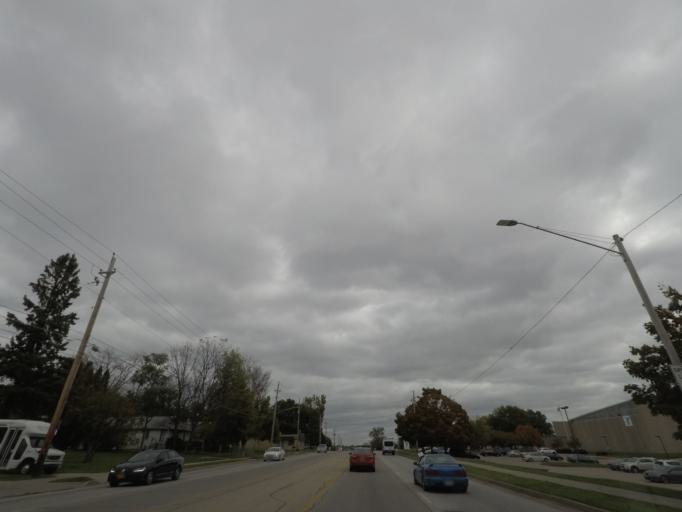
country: US
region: Iowa
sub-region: Polk County
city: Des Moines
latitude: 41.5264
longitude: -93.6106
